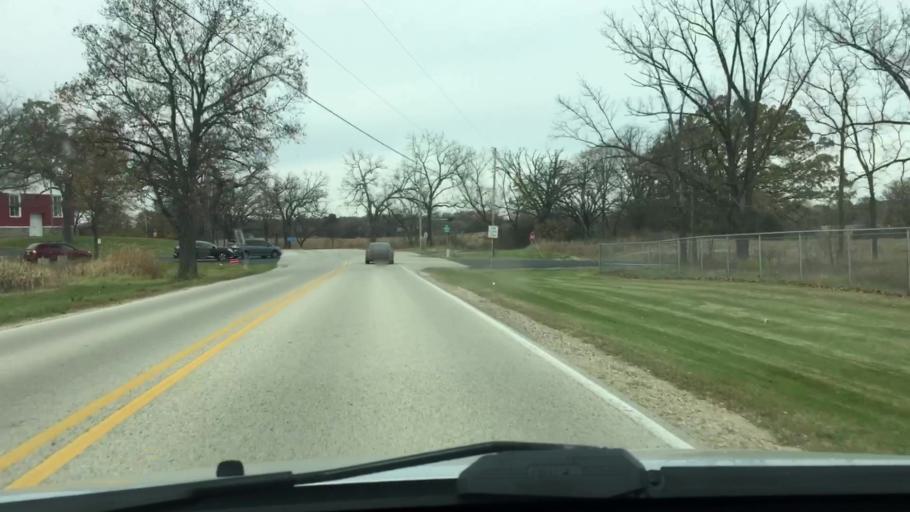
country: US
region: Wisconsin
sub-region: Waukesha County
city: North Prairie
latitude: 42.8930
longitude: -88.3845
